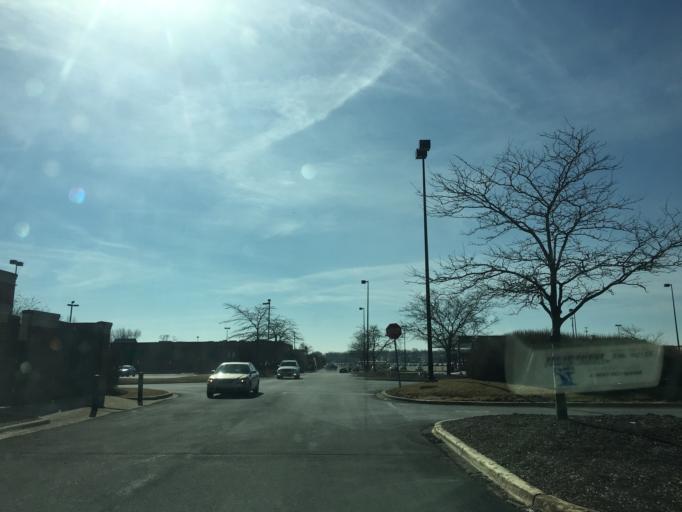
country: US
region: Illinois
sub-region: DuPage County
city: Hanover Park
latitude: 42.0148
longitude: -88.1455
